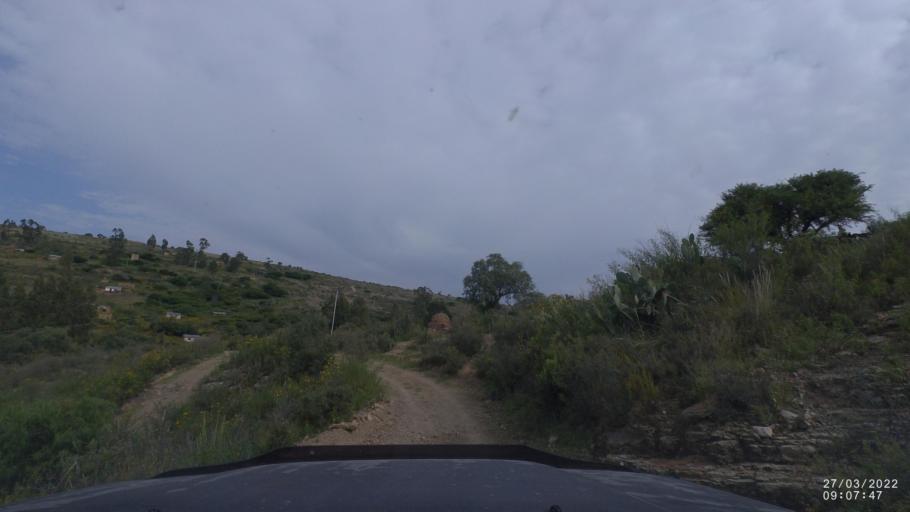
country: BO
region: Cochabamba
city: Cliza
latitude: -17.7319
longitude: -65.8734
